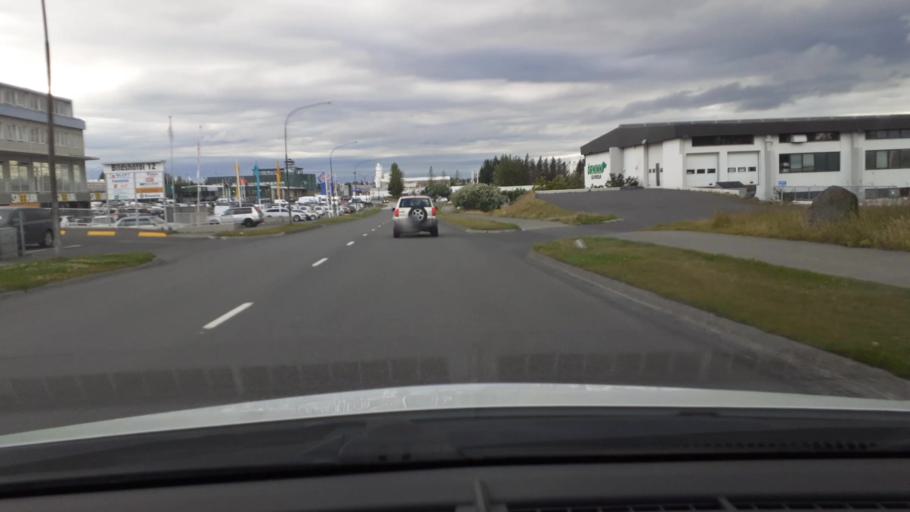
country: IS
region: Capital Region
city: Reykjavik
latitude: 64.1256
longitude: -21.8193
